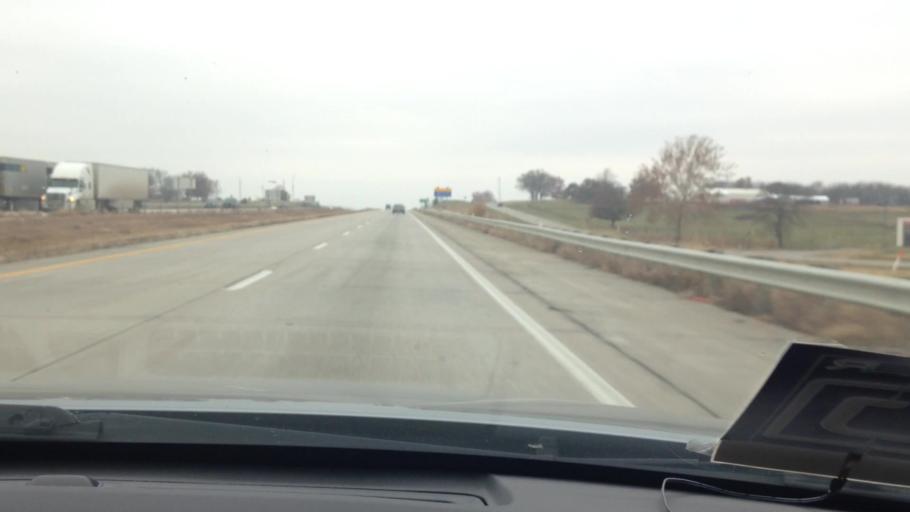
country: US
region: Missouri
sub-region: Cass County
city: Harrisonville
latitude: 38.6631
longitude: -94.3783
